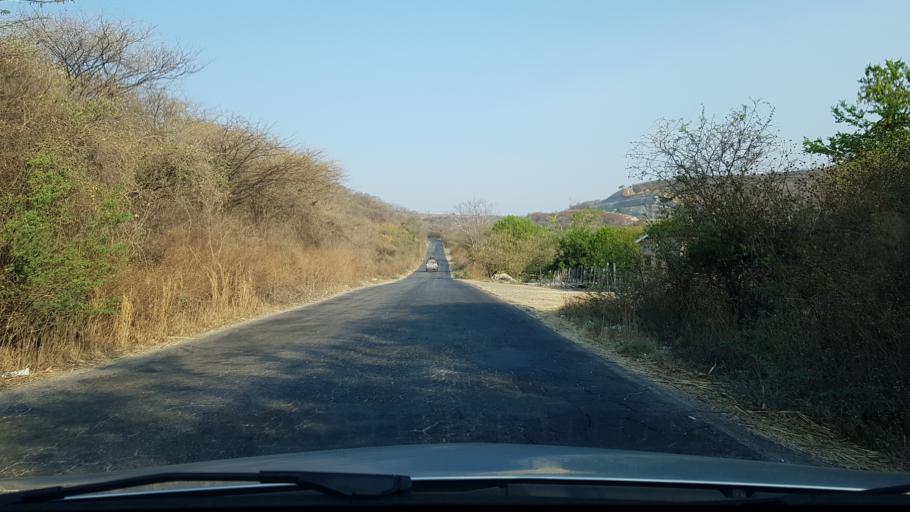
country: MX
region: Morelos
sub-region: Tepalcingo
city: Zacapalco
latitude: 18.6550
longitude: -99.0377
